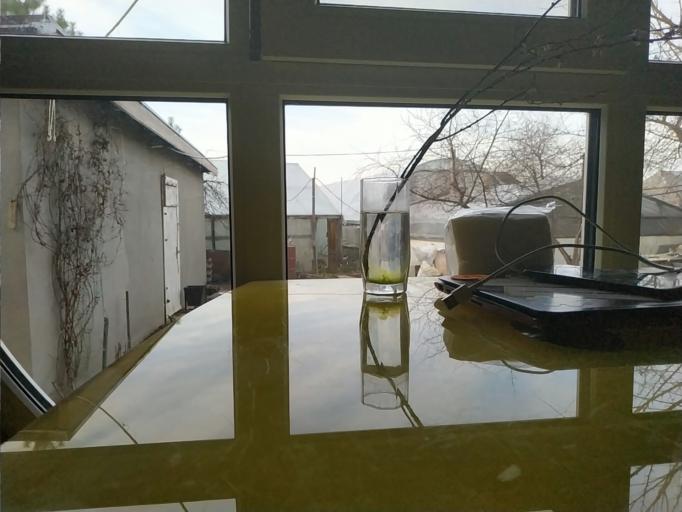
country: RU
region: Republic of Karelia
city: Suoyarvi
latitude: 61.8465
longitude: 32.2798
